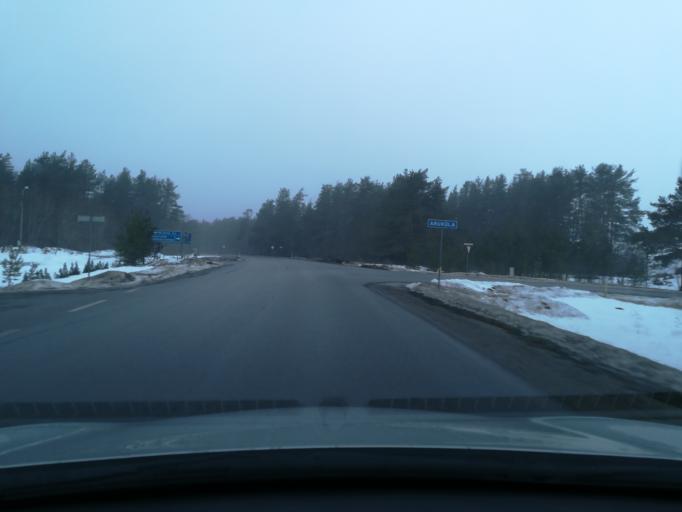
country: EE
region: Harju
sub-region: Raasiku vald
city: Arukula
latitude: 59.3557
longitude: 25.0761
